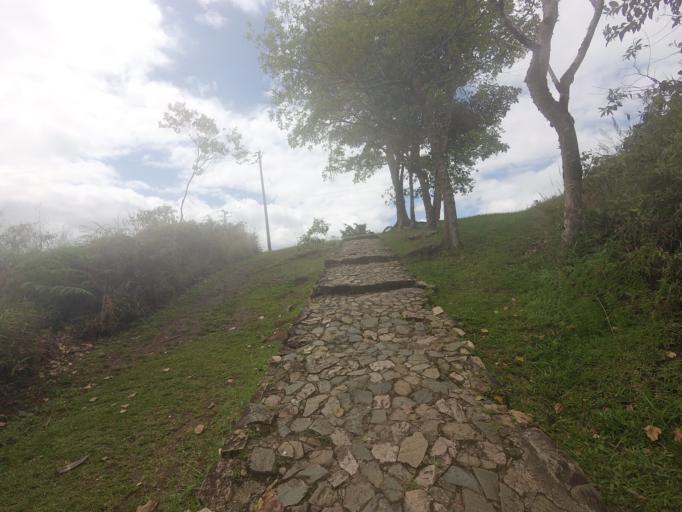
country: CO
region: Huila
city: San Agustin
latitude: 1.8808
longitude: -76.3027
